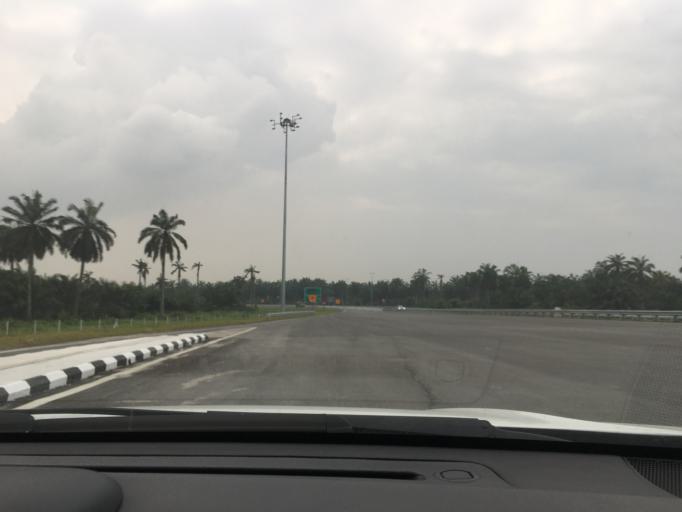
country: MY
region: Selangor
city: Klang
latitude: 3.1302
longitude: 101.3983
